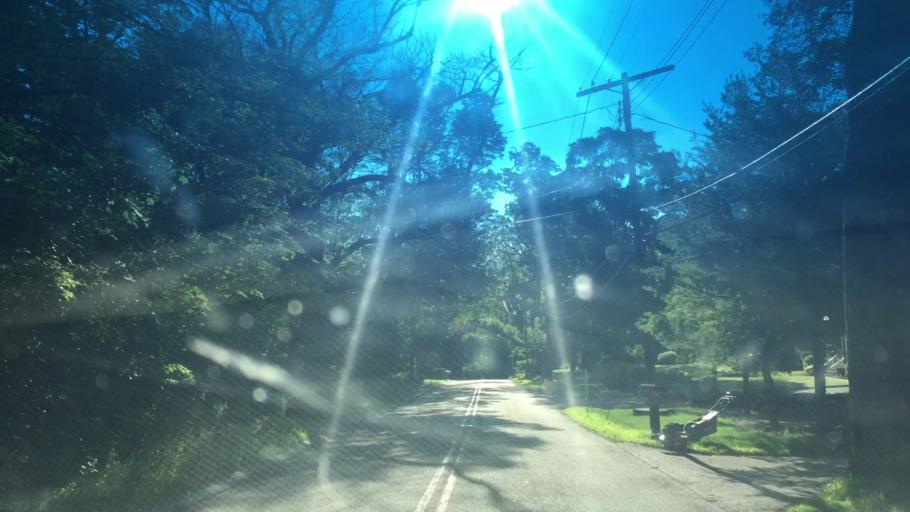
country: US
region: Massachusetts
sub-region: Norfolk County
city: Millis-Clicquot
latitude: 42.1450
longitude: -71.3567
